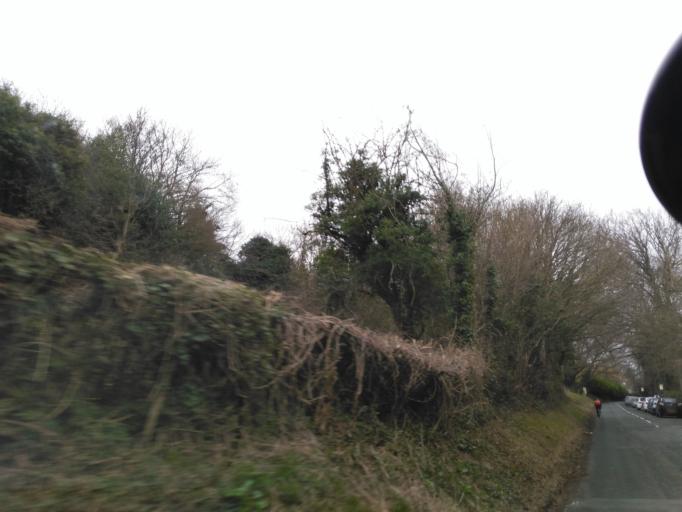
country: GB
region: England
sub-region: Bath and North East Somerset
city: Bath
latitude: 51.3838
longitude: -2.3409
